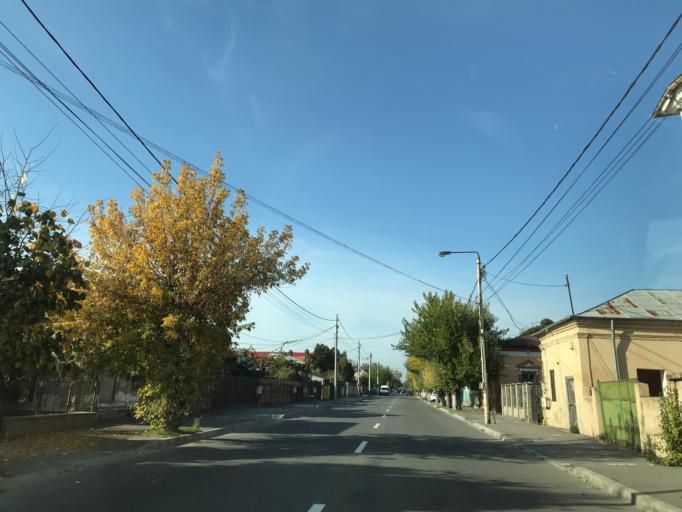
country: RO
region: Olt
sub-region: Municipiul Slatina
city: Slatina
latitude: 44.4364
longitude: 24.3491
